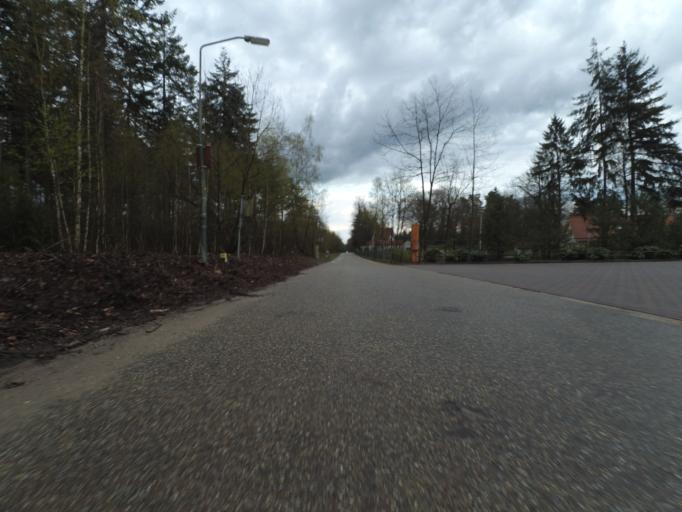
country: NL
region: Gelderland
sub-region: Gemeente Apeldoorn
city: Beekbergen
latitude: 52.1335
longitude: 5.9455
